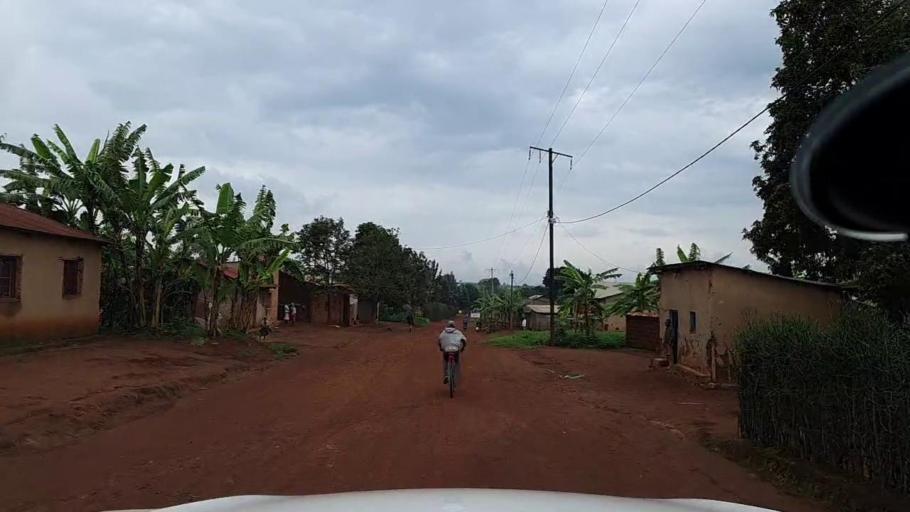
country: RW
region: Kigali
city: Kigali
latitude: -1.9211
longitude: 29.8989
